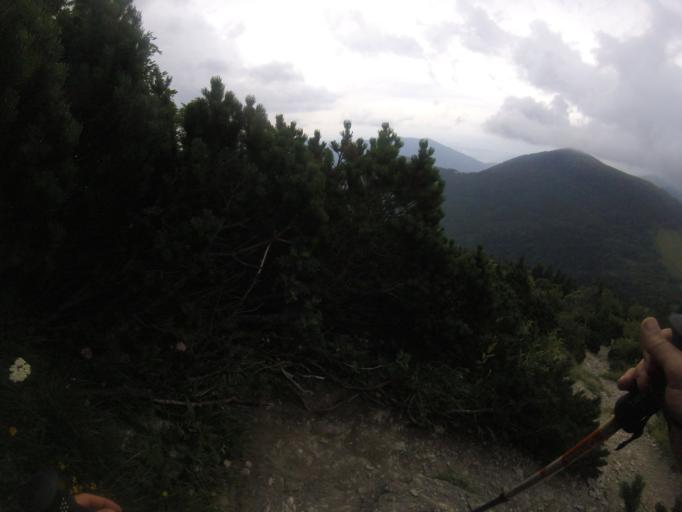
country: SK
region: Zilinsky
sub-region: Okres Zilina
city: Terchova
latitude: 49.2292
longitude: 19.1021
